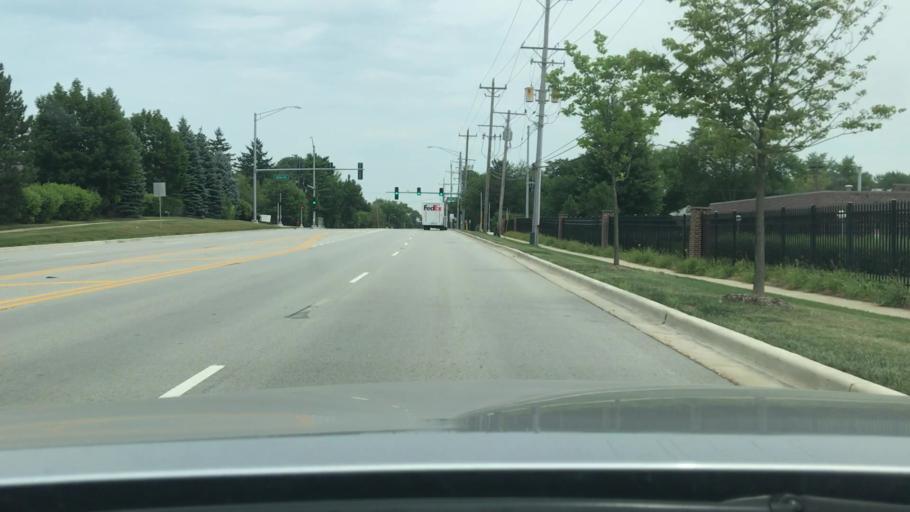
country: US
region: Illinois
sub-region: DuPage County
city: Darien
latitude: 41.7464
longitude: -87.9813
